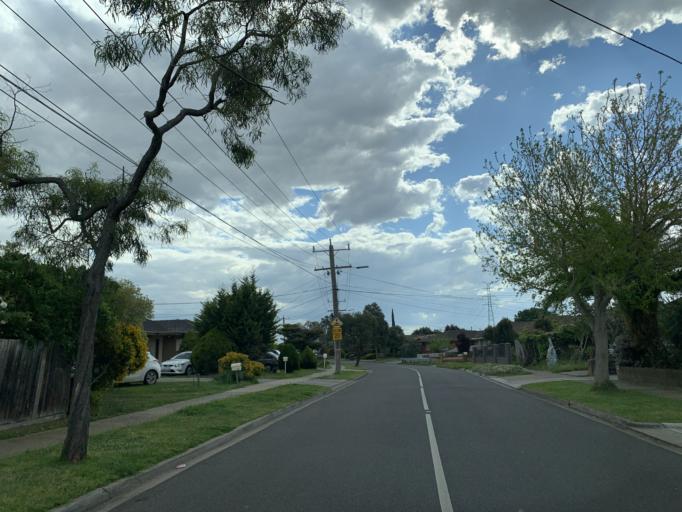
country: AU
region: Victoria
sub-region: Moonee Valley
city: Keilor East
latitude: -37.7409
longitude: 144.8545
